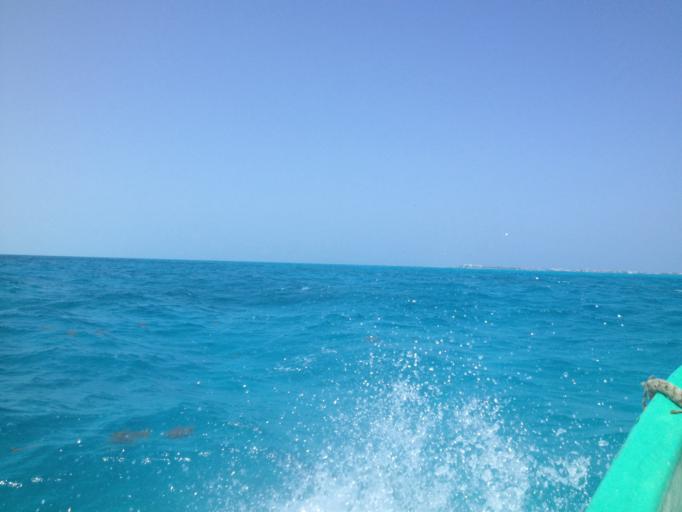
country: MX
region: Quintana Roo
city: Isla Mujeres
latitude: 21.2210
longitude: -86.7733
